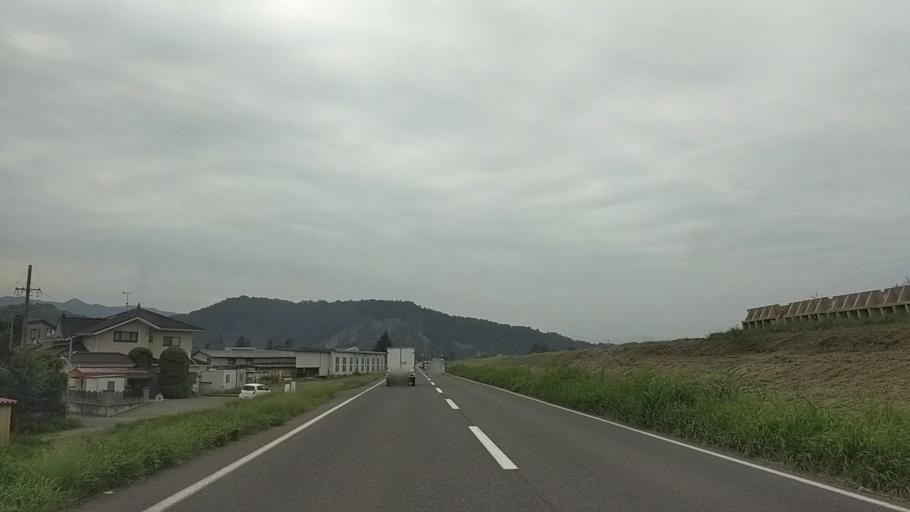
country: JP
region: Nagano
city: Nagano-shi
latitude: 36.5961
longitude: 138.2163
